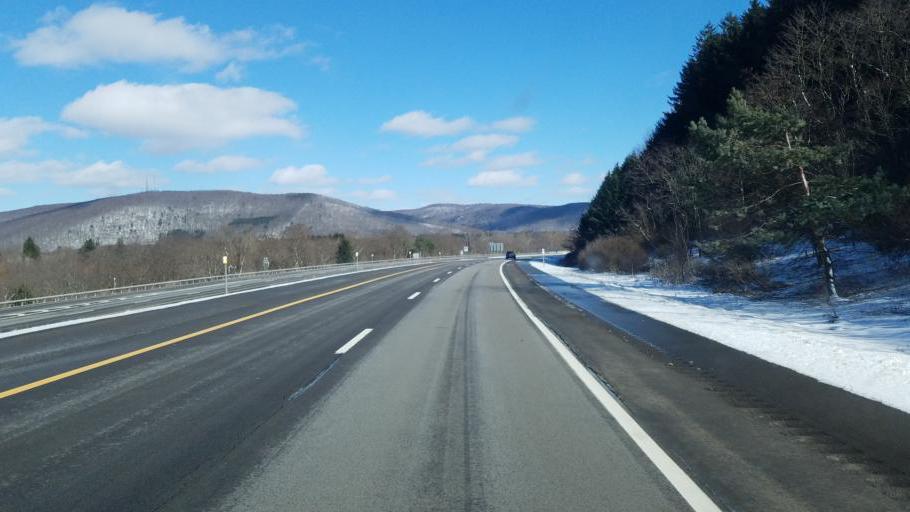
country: US
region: New York
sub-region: Cattaraugus County
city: Salamanca
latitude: 42.1512
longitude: -78.7018
